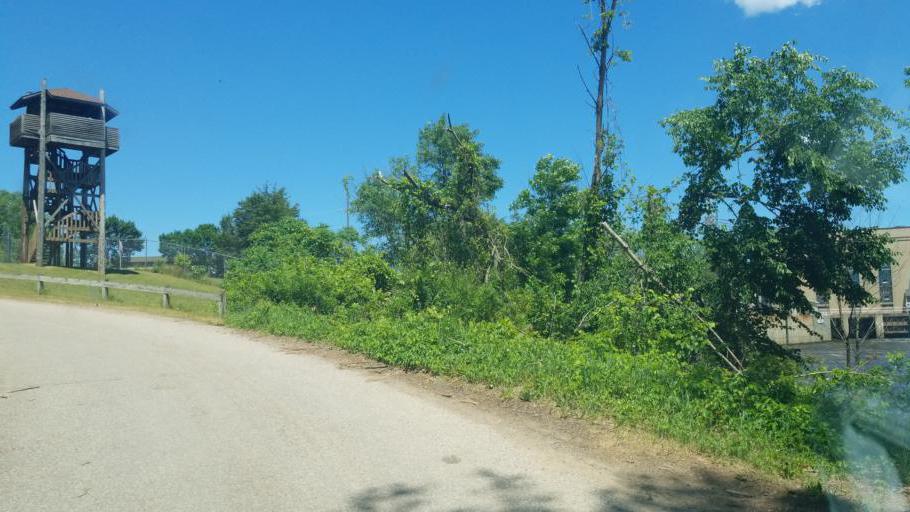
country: US
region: Wisconsin
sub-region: Adams County
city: Friendship
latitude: 44.0559
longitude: -90.0223
